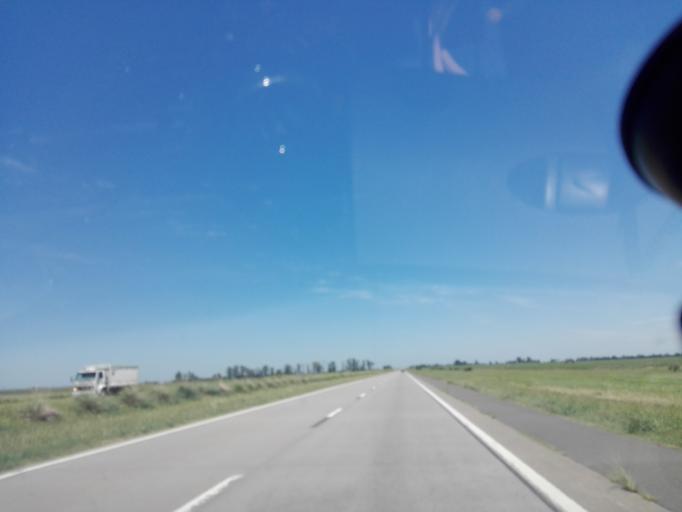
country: AR
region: Santa Fe
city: Armstrong
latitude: -32.7939
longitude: -61.6949
